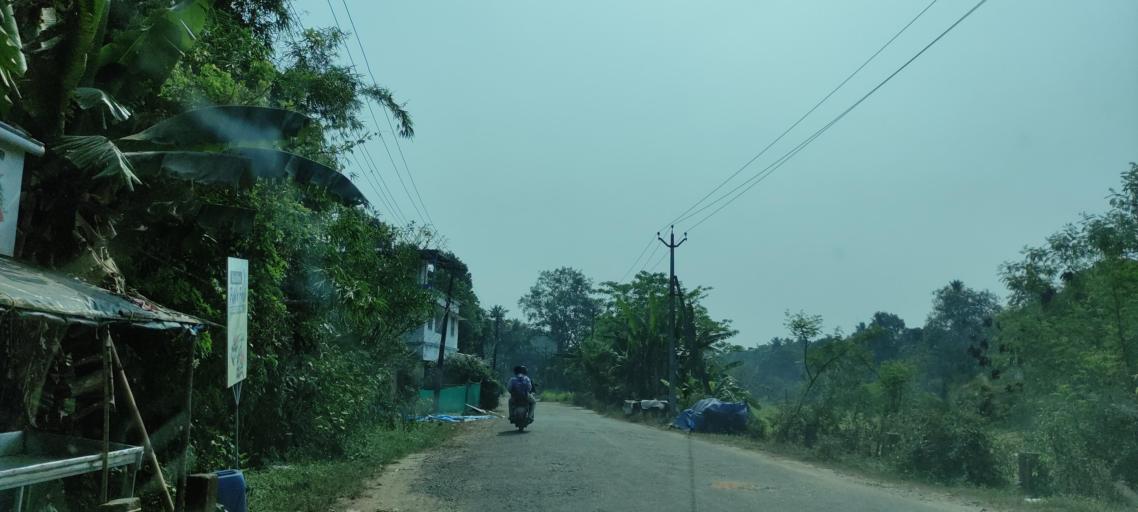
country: IN
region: Kerala
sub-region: Pattanamtitta
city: Tiruvalla
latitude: 9.3490
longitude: 76.5505
